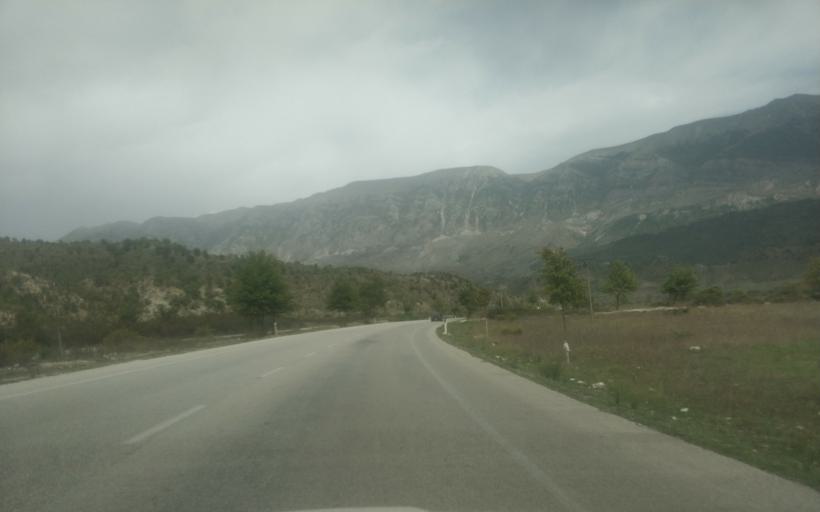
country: AL
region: Gjirokaster
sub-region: Rrethi i Gjirokastres
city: Picar
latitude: 40.1959
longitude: 20.0830
